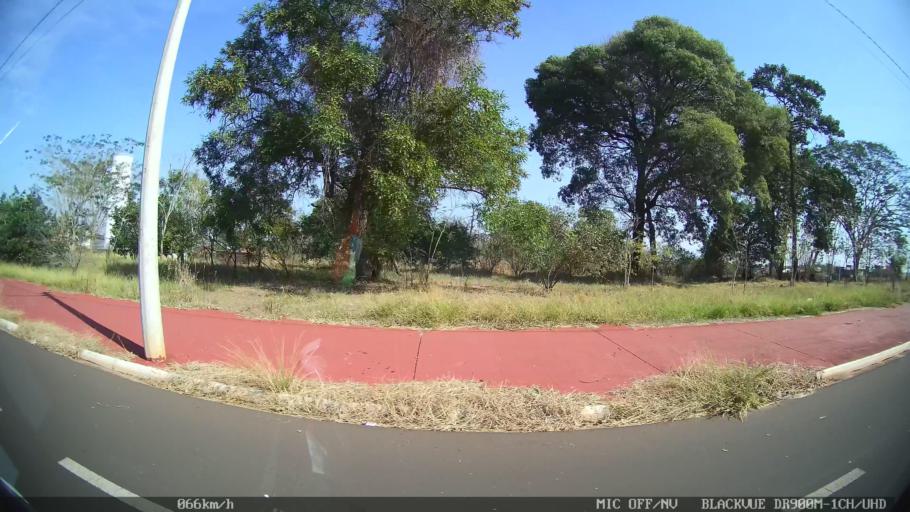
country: BR
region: Sao Paulo
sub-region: Sao Jose Do Rio Preto
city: Sao Jose do Rio Preto
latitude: -20.7850
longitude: -49.4256
